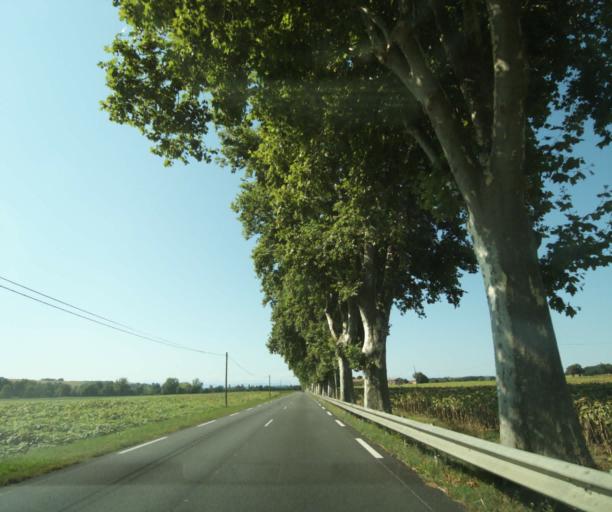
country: FR
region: Midi-Pyrenees
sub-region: Departement de la Haute-Garonne
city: Saint-Sulpice-sur-Leze
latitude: 43.3587
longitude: 1.3278
